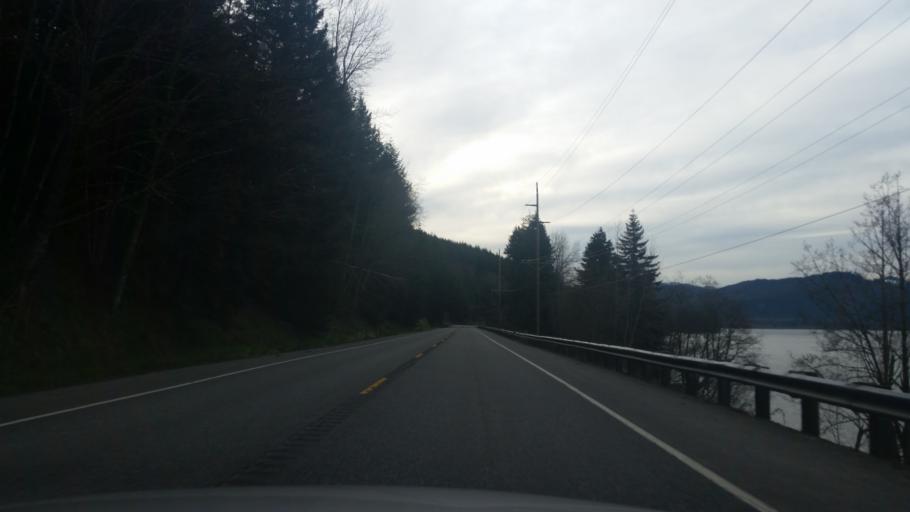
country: US
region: Washington
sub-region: Pierce County
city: Eatonville
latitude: 46.7816
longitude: -122.2373
